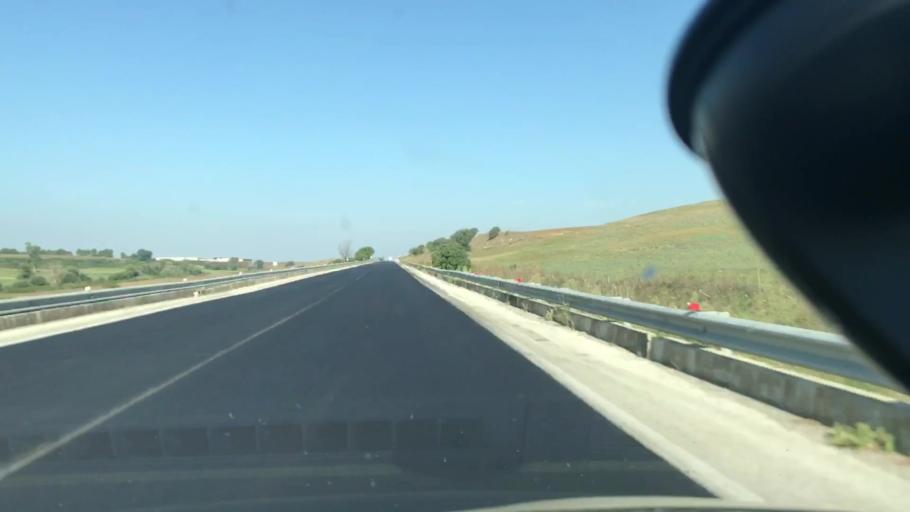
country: IT
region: Apulia
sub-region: Provincia di Barletta - Andria - Trani
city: Spinazzola
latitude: 40.9031
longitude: 16.1169
